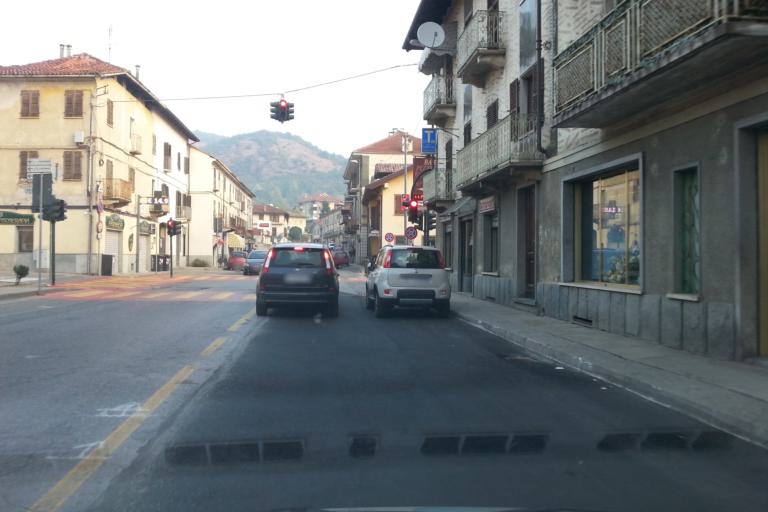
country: IT
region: Piedmont
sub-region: Provincia di Torino
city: Trana
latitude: 45.0367
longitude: 7.4196
